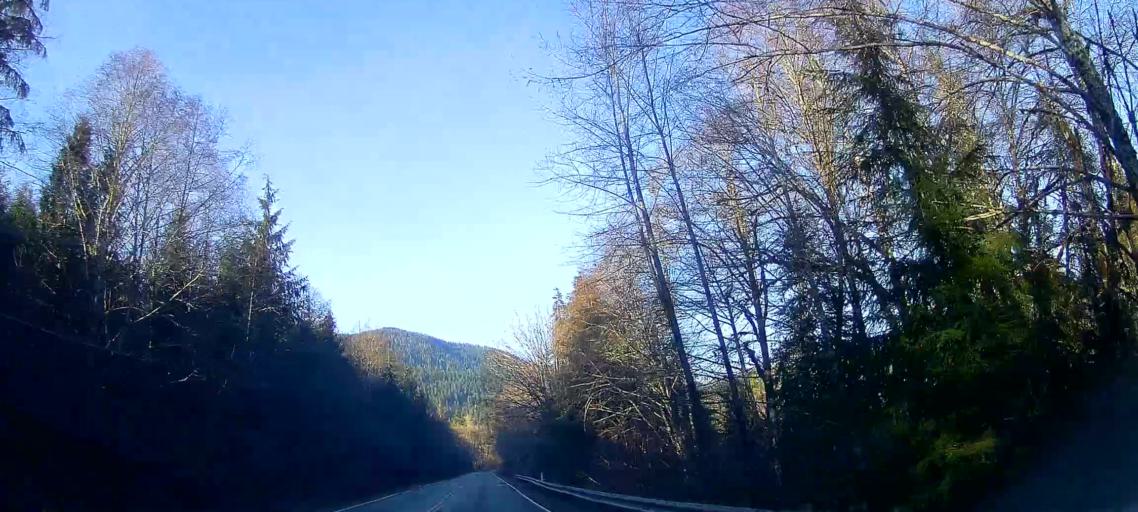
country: US
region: Washington
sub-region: Snohomish County
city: Darrington
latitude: 48.6307
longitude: -121.7390
